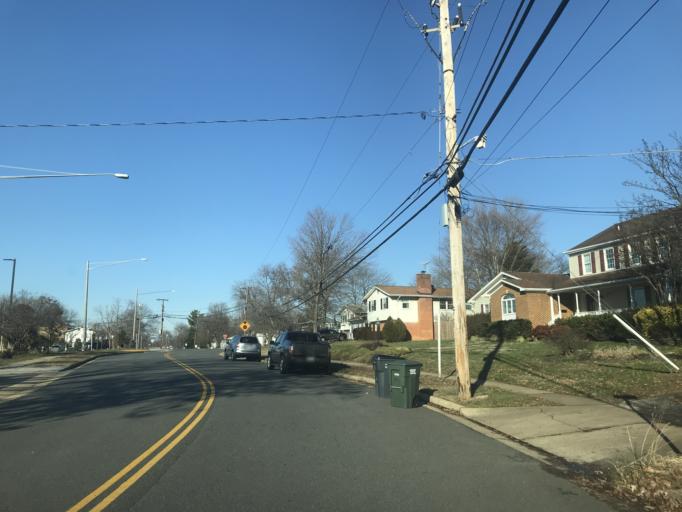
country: US
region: Virginia
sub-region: Fairfax County
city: Franconia
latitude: 38.7829
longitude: -77.1633
